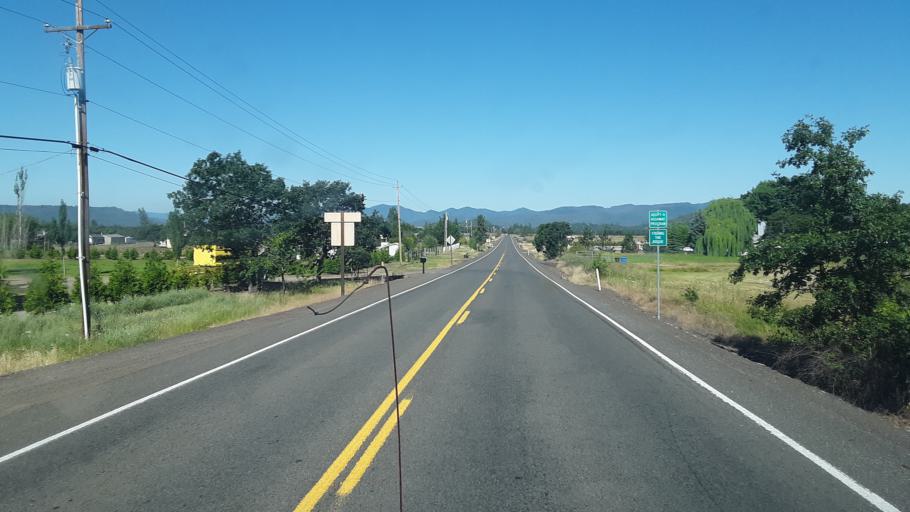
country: US
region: Oregon
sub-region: Jackson County
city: Eagle Point
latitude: 42.5235
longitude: -122.8151
